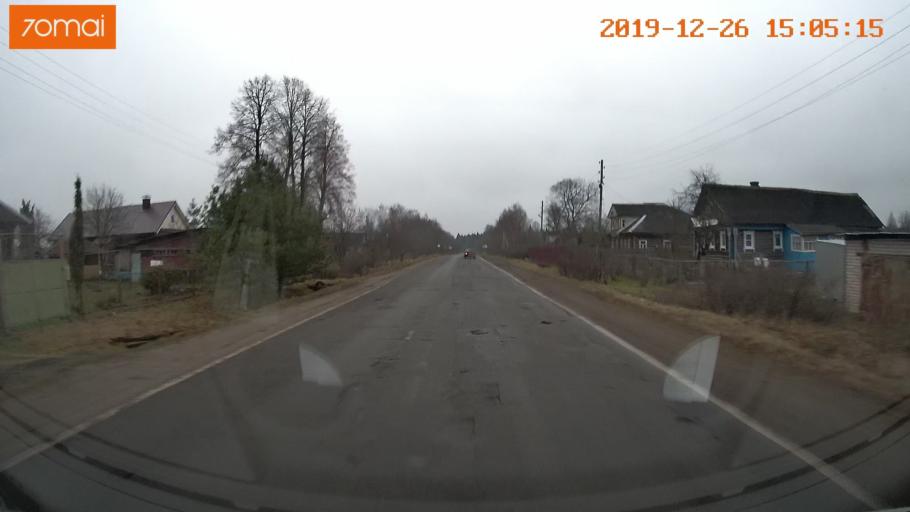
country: RU
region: Jaroslavl
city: Rybinsk
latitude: 58.1910
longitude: 38.8534
